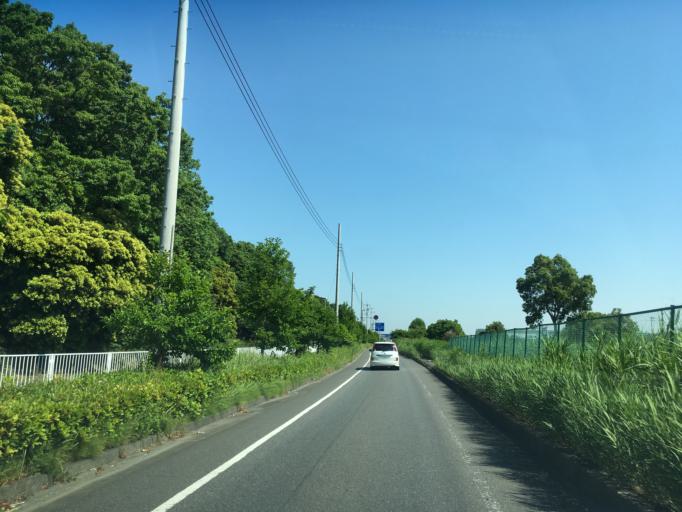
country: JP
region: Saitama
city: Yoshikawa
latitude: 35.8607
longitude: 139.8297
